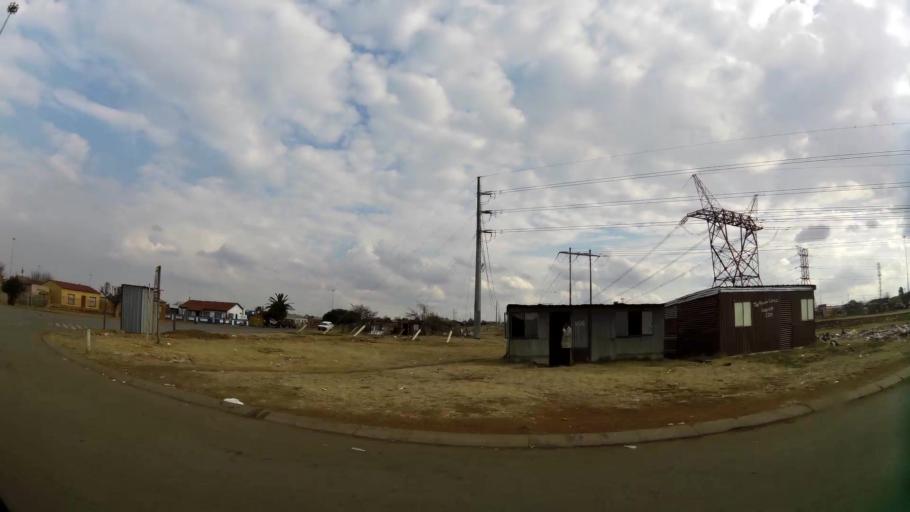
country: ZA
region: Gauteng
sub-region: Sedibeng District Municipality
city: Vereeniging
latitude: -26.6732
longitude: 27.8786
